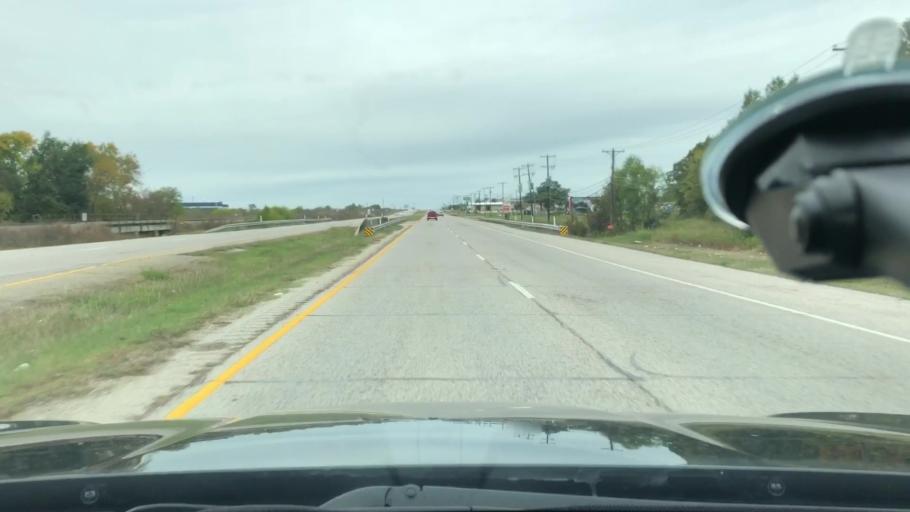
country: US
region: Texas
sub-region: Kaufman County
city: Terrell
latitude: 32.7372
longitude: -96.3079
